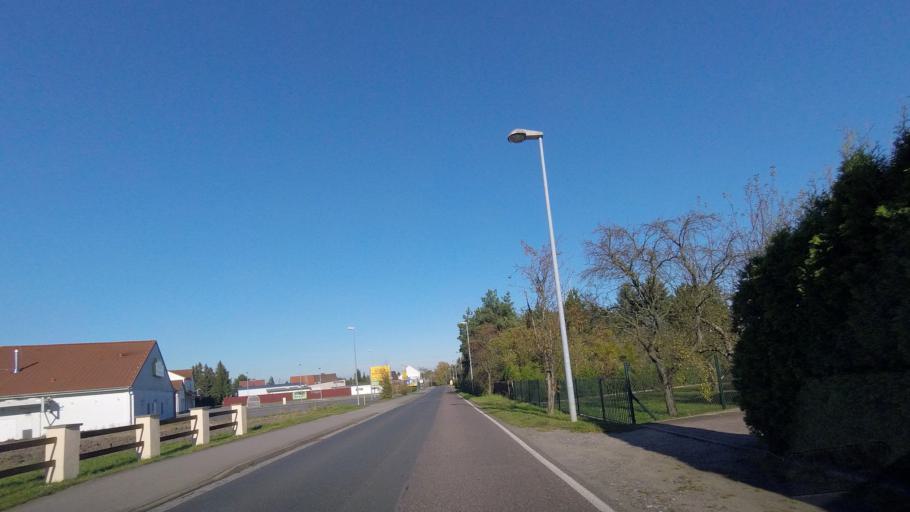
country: DE
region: Saxony-Anhalt
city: Zahna
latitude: 51.9128
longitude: 12.7801
